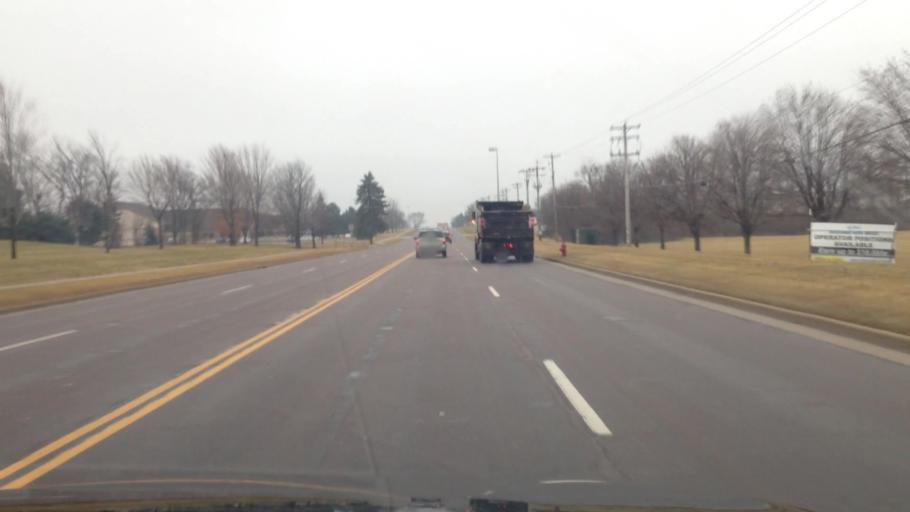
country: US
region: Wisconsin
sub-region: Washington County
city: Germantown
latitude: 43.2300
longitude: -88.1428
